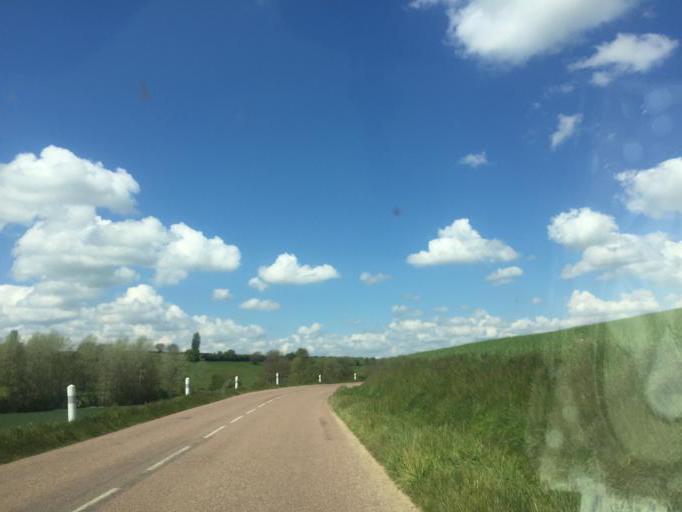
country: FR
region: Bourgogne
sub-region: Departement de la Nievre
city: Clamecy
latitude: 47.4614
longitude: 3.4558
